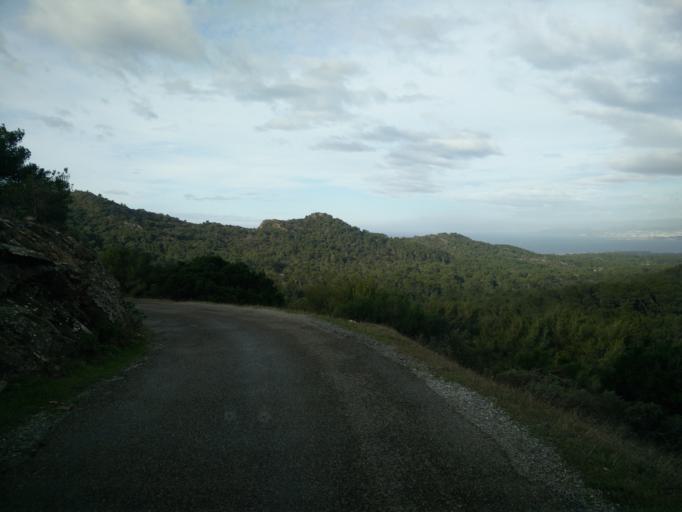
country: FR
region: Provence-Alpes-Cote d'Azur
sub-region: Departement du Var
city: Six-Fours-les-Plages
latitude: 43.0594
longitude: 5.8398
